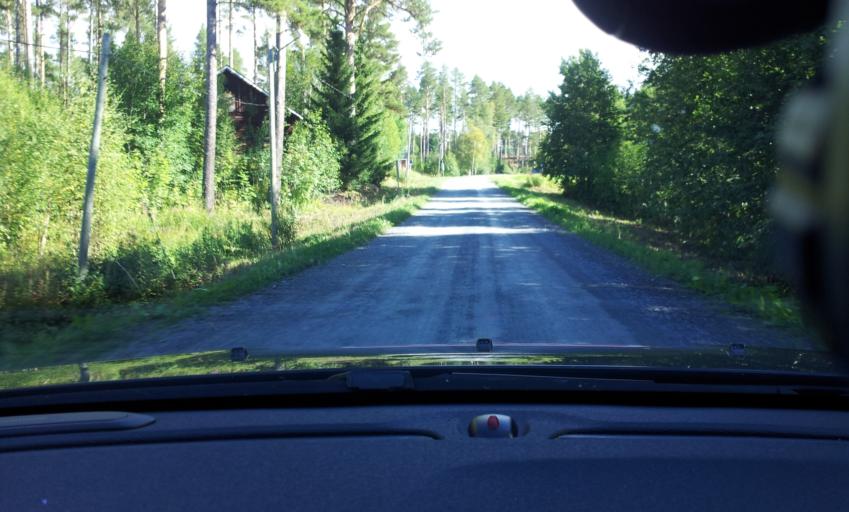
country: SE
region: Jaemtland
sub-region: Are Kommun
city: Jarpen
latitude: 63.2842
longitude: 13.7331
